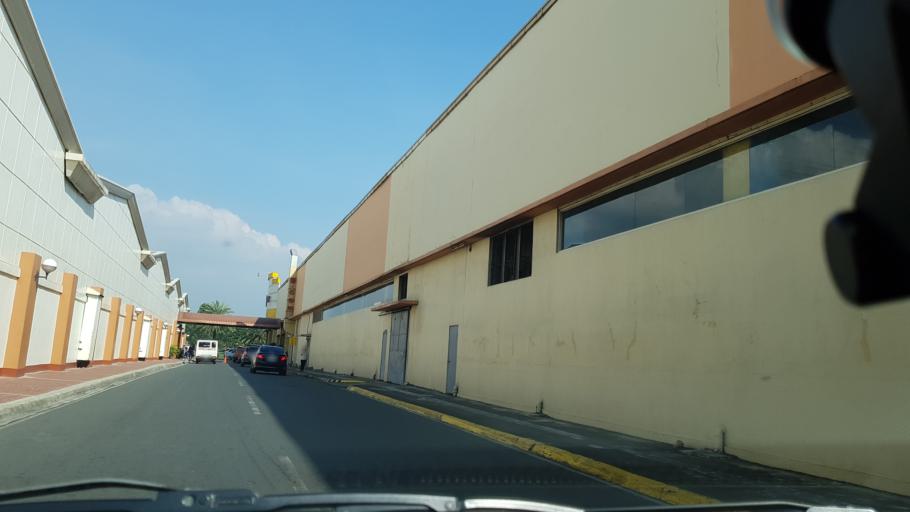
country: PH
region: Metro Manila
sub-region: Marikina
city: Calumpang
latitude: 14.6299
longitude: 121.0813
